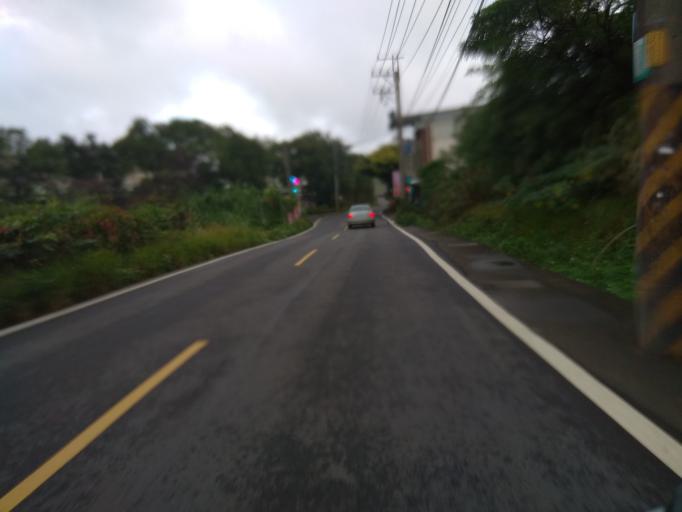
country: TW
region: Taiwan
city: Daxi
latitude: 24.9240
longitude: 121.1516
